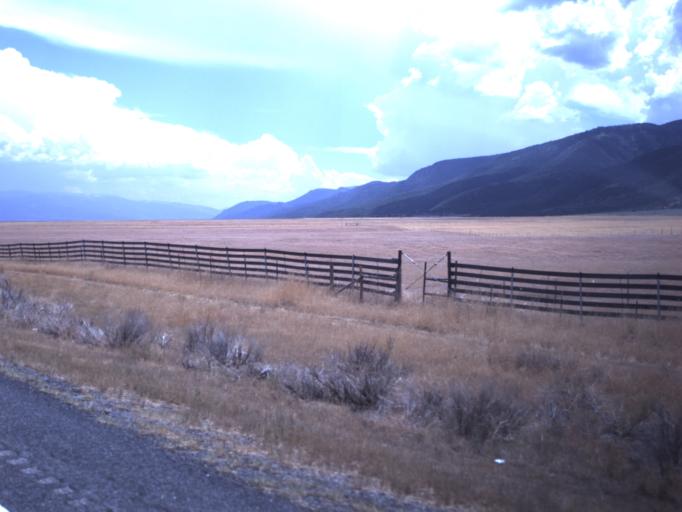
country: US
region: Utah
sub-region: Sanpete County
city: Fountain Green
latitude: 39.6666
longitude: -111.6600
